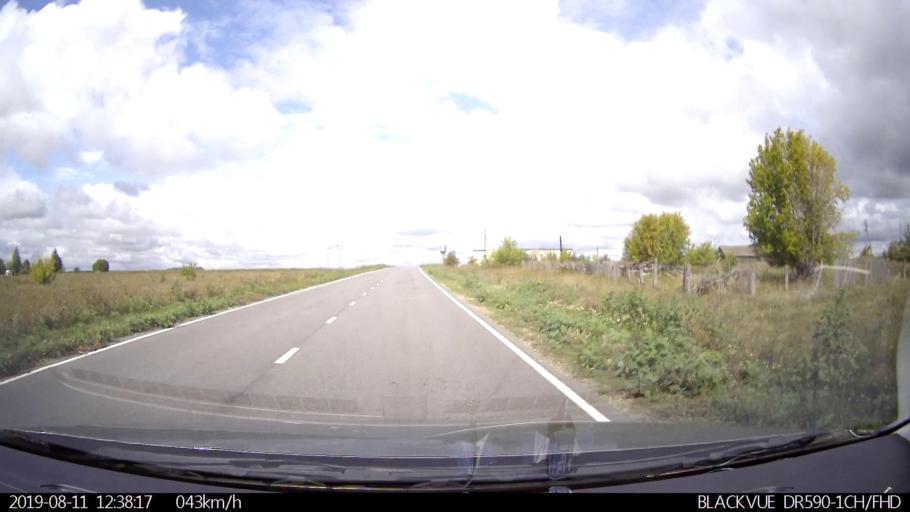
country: RU
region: Ulyanovsk
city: Ignatovka
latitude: 53.8261
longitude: 47.8078
